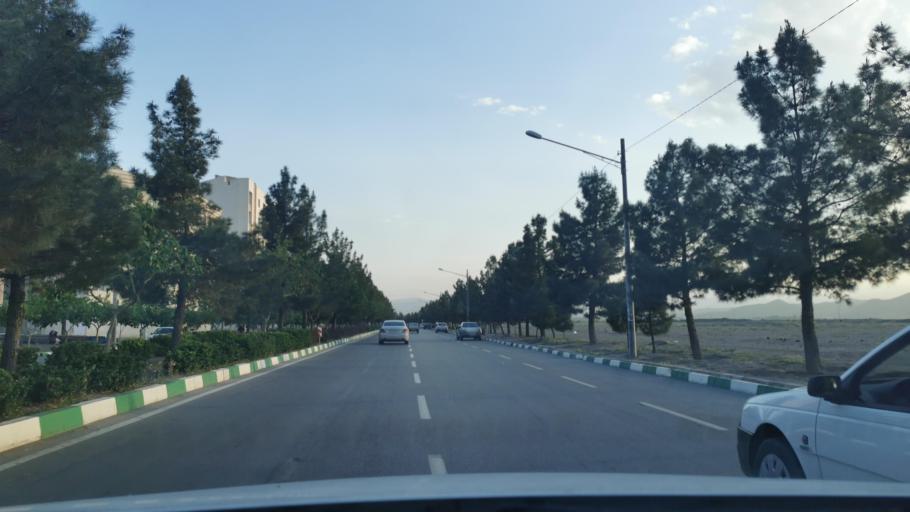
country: IR
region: Razavi Khorasan
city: Mashhad
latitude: 36.3902
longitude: 59.4691
